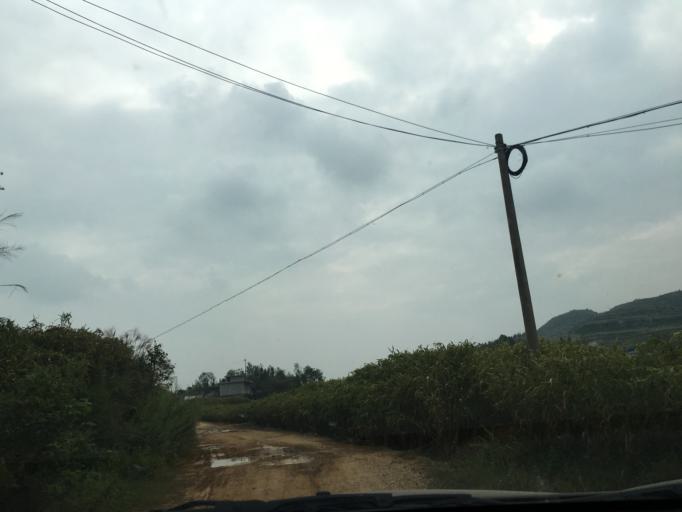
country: CN
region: Guangxi Zhuangzu Zizhiqu
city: Xinzhou
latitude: 25.5412
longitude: 105.5318
